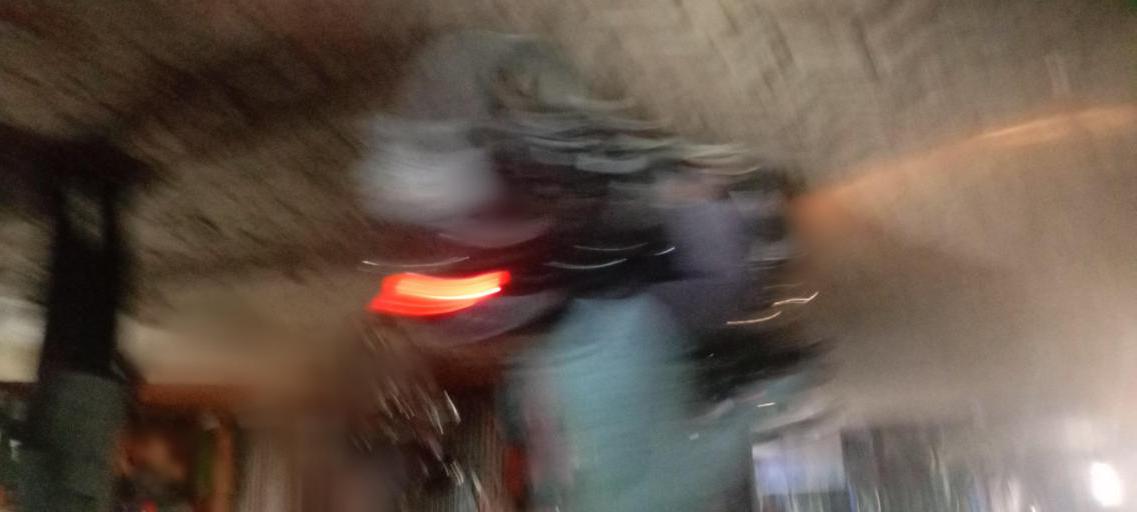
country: BD
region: Dhaka
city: Sakhipur
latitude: 24.4514
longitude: 90.2791
